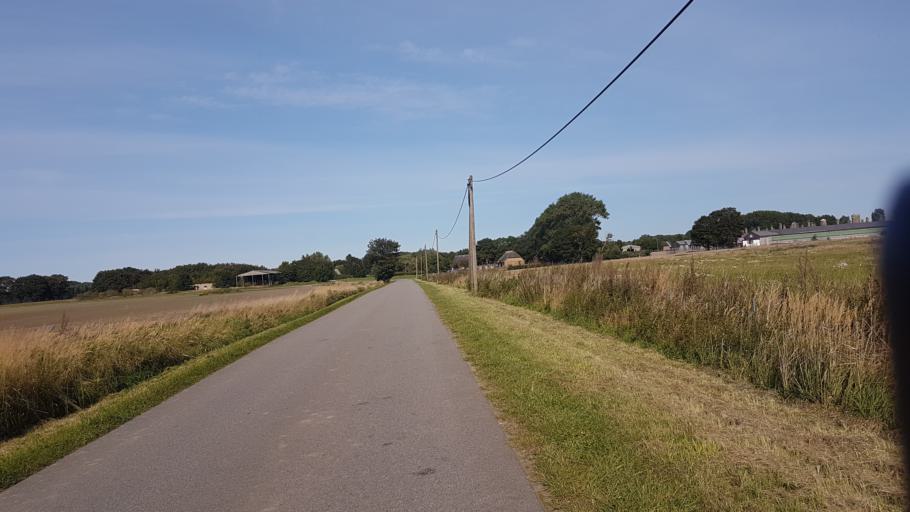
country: DE
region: Mecklenburg-Vorpommern
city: Gingst
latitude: 54.4322
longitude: 13.2236
